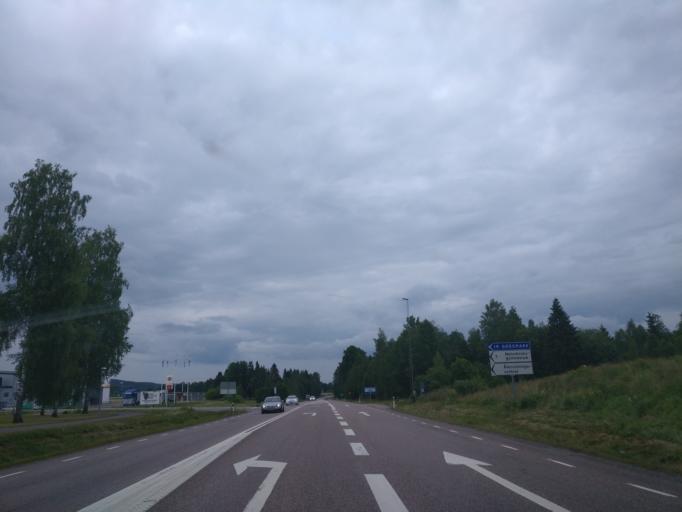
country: SE
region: Vaermland
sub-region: Sunne Kommun
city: Sunne
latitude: 59.8533
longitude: 13.1256
